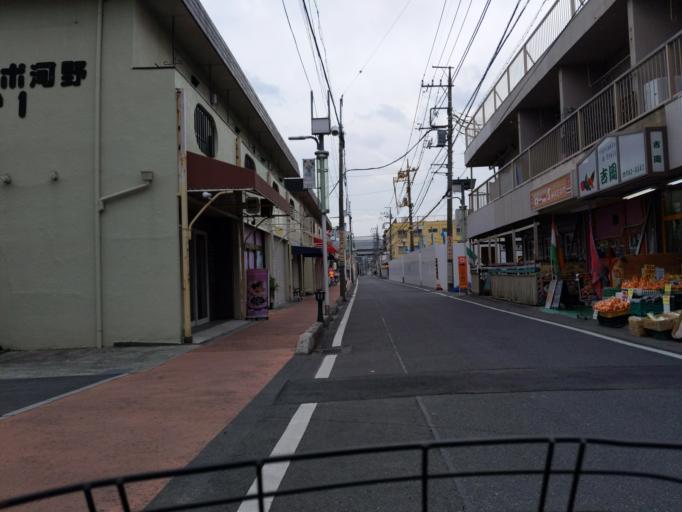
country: JP
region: Saitama
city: Koshigaya
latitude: 35.8521
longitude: 139.7947
